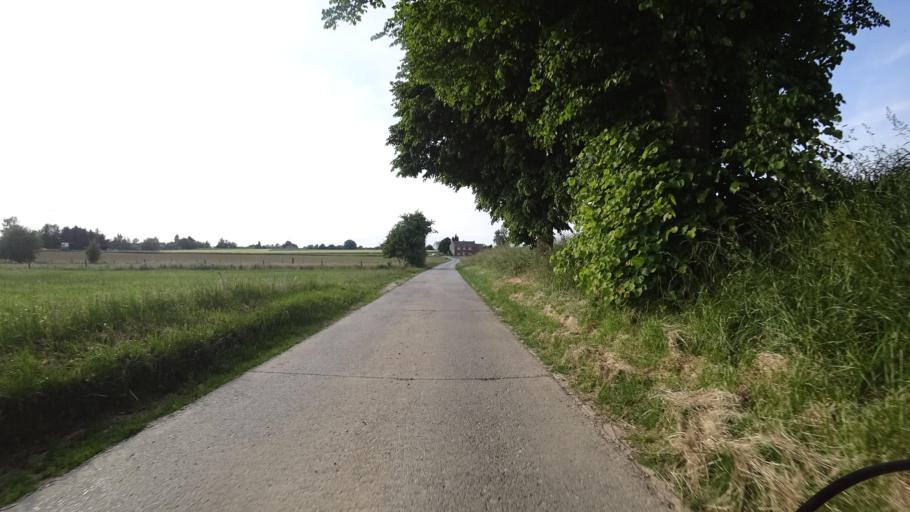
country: BE
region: Wallonia
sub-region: Province du Brabant Wallon
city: Perwez
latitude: 50.5397
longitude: 4.7936
